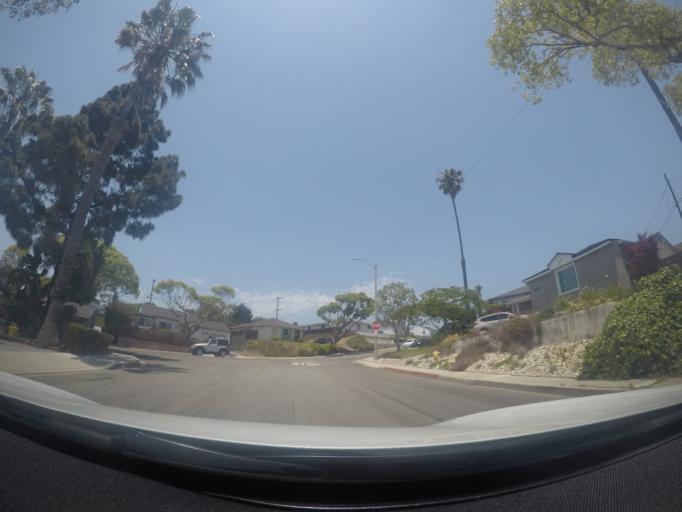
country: US
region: California
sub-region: Los Angeles County
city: Palos Verdes Estates
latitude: 33.8225
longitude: -118.3706
